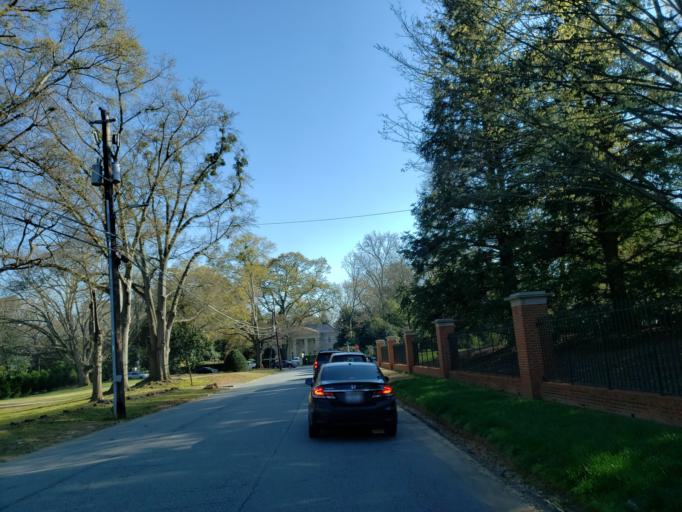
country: US
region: Georgia
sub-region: DeKalb County
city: North Atlanta
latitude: 33.8455
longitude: -84.3977
